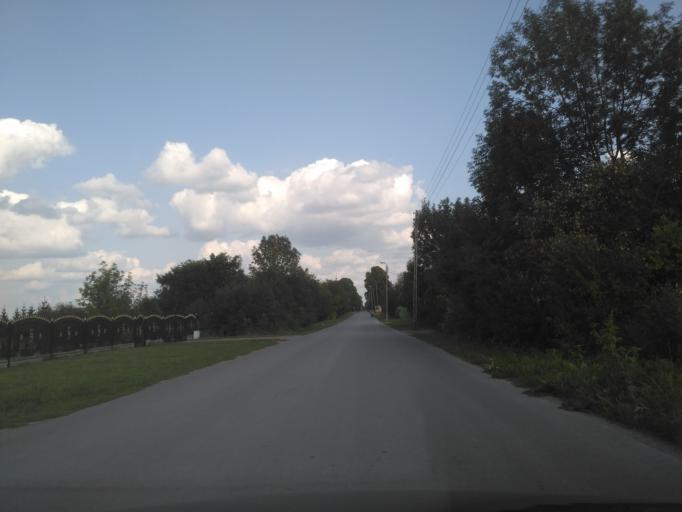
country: PL
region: Lublin Voivodeship
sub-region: Powiat chelmski
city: Pokrowka
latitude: 51.0679
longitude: 23.4872
